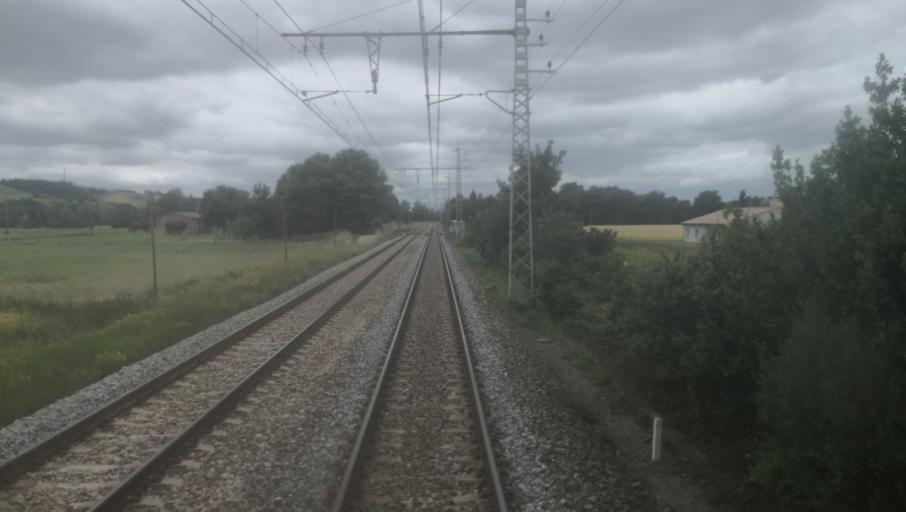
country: FR
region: Midi-Pyrenees
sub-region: Departement de la Haute-Garonne
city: Avignonet-Lauragais
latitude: 43.3679
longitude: 1.7730
